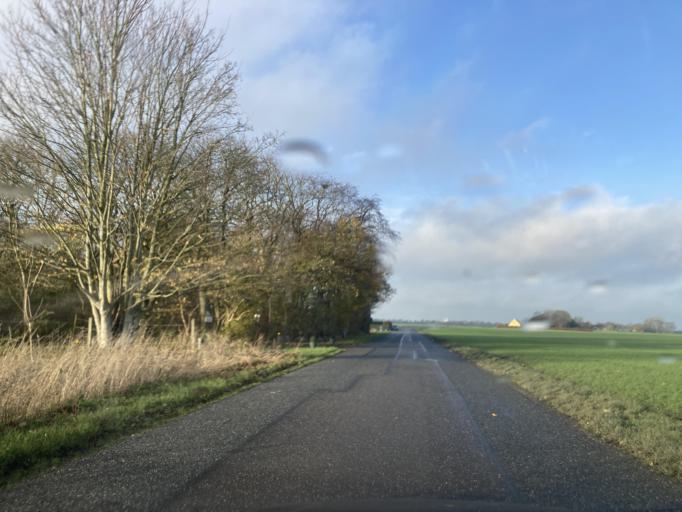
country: DK
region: Zealand
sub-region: Lolland Kommune
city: Rodby
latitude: 54.6810
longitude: 11.4139
